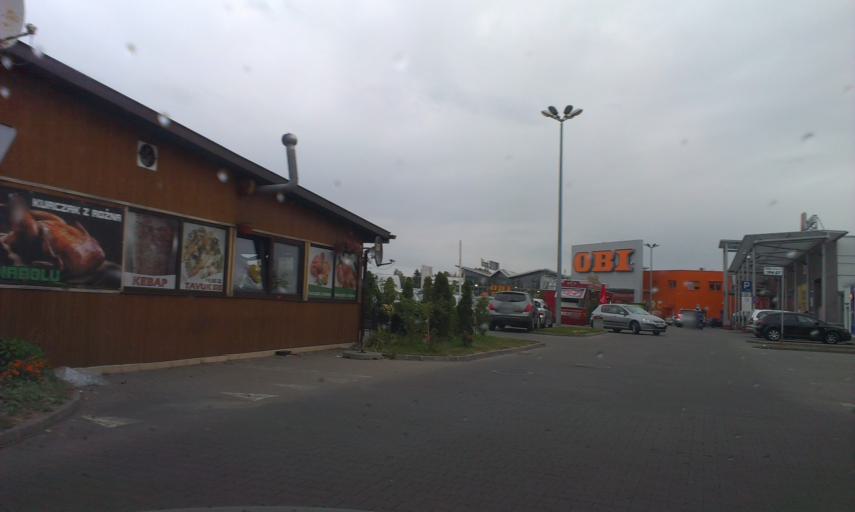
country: PL
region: Masovian Voivodeship
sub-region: Radom
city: Radom
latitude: 51.4078
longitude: 21.1423
